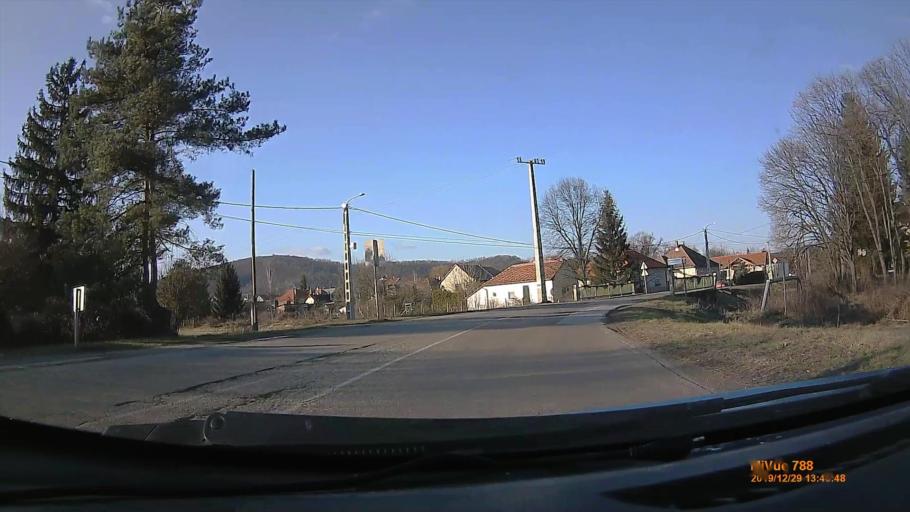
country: HU
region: Heves
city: Recsk
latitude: 47.9331
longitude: 20.1189
